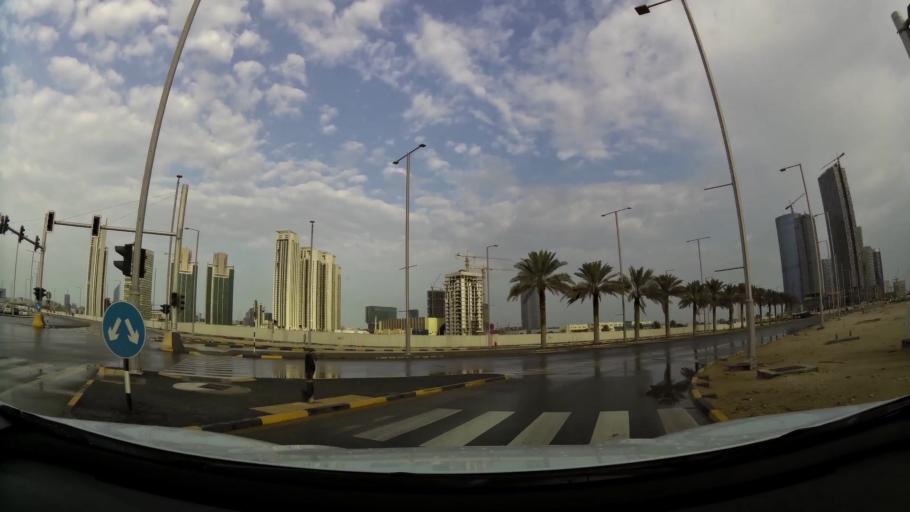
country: AE
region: Abu Dhabi
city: Abu Dhabi
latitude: 24.4878
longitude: 54.4032
